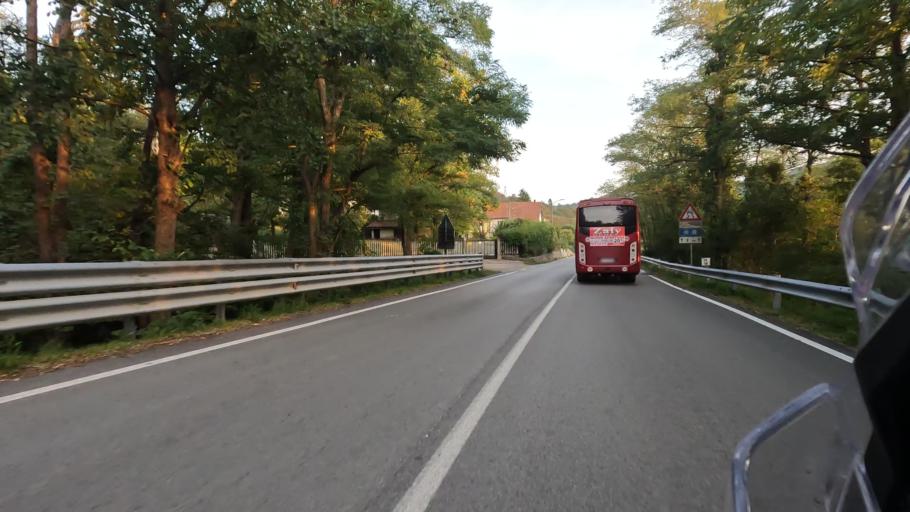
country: IT
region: Liguria
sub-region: Provincia di Savona
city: Pontinvrea
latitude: 44.4355
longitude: 8.4523
